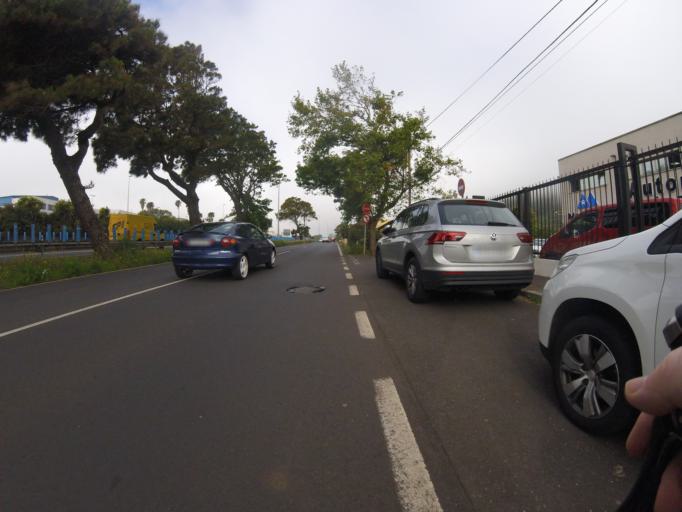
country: ES
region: Canary Islands
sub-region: Provincia de Santa Cruz de Tenerife
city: La Laguna
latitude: 28.4896
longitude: -16.3429
